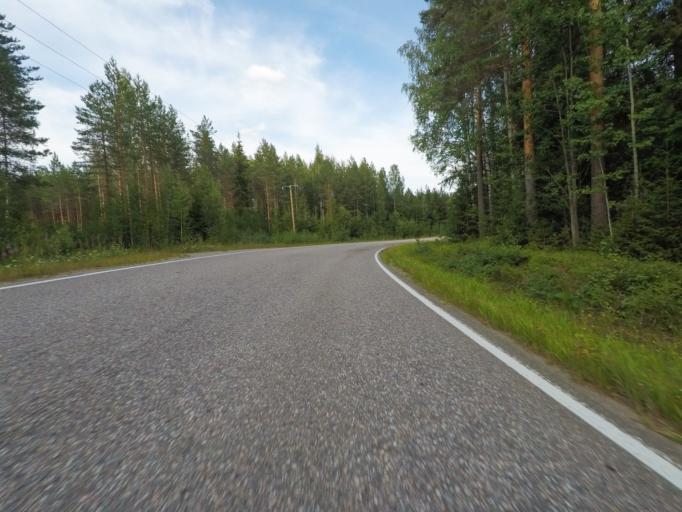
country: FI
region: Southern Savonia
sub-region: Savonlinna
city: Sulkava
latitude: 61.7533
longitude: 28.2160
